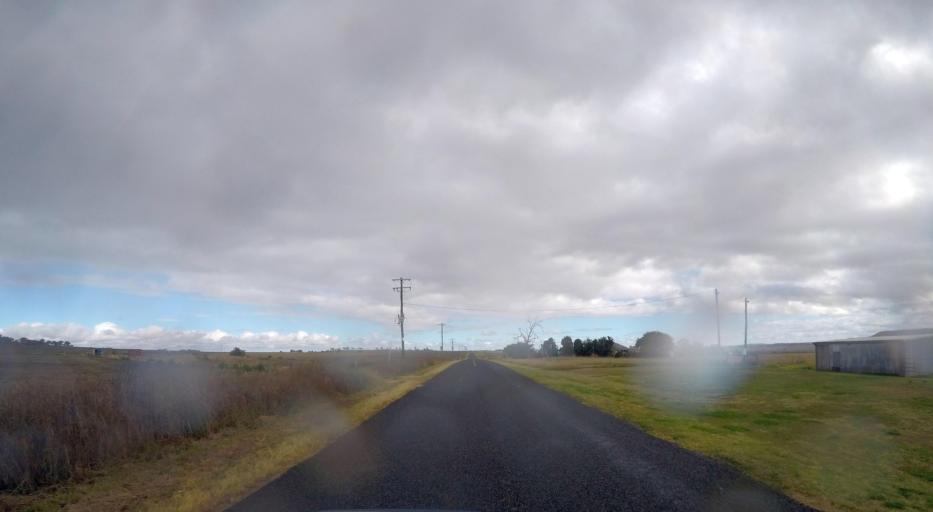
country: AU
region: Queensland
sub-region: Southern Downs
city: Warwick
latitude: -28.0513
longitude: 152.0335
